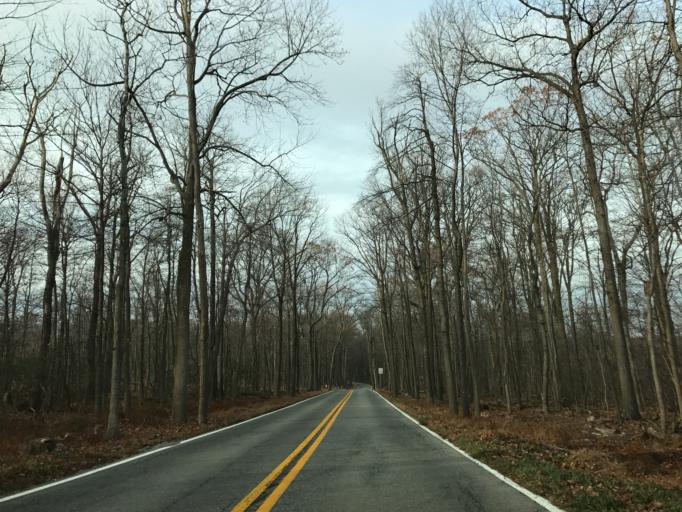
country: US
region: Maryland
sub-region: Frederick County
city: Myersville
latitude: 39.5019
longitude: -77.4997
